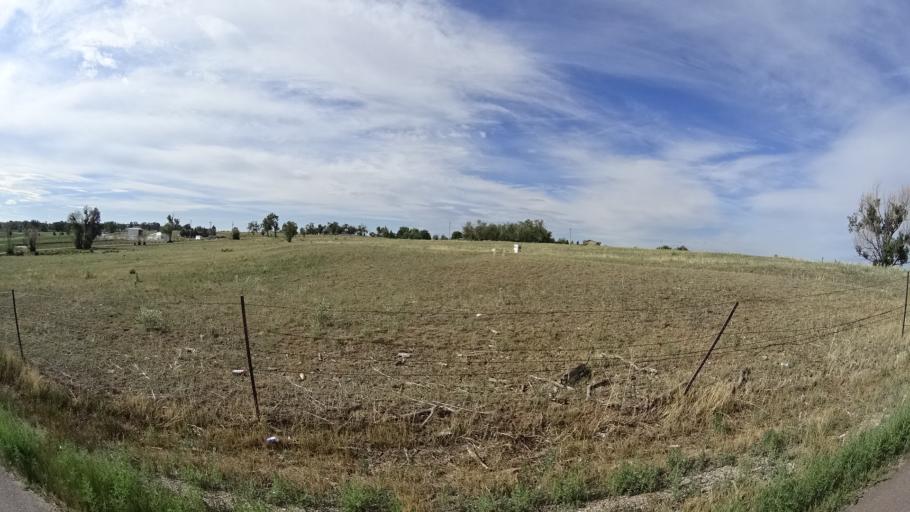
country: US
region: Colorado
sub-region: El Paso County
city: Fountain
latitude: 38.6865
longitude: -104.6751
